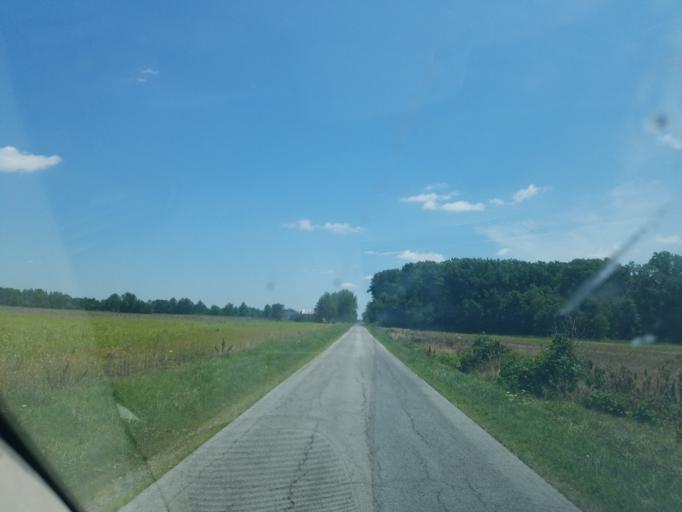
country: US
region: Ohio
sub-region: Hancock County
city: Arlington
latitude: 40.8484
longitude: -83.6298
